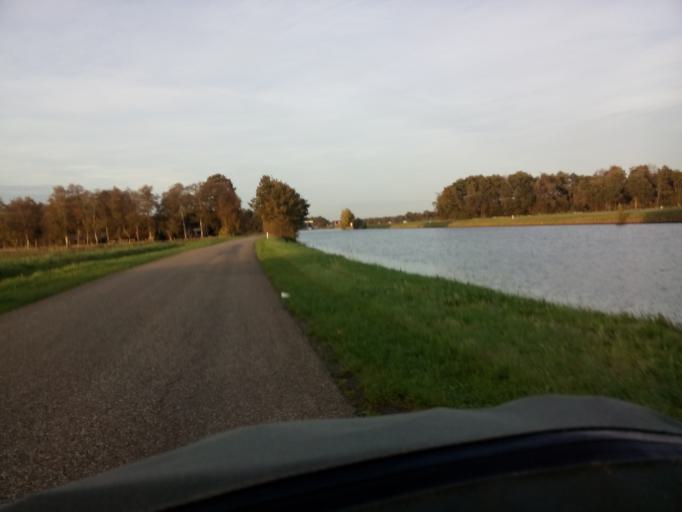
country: NL
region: Drenthe
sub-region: Gemeente Tynaarlo
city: Tynaarlo
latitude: 53.0312
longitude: 6.6015
